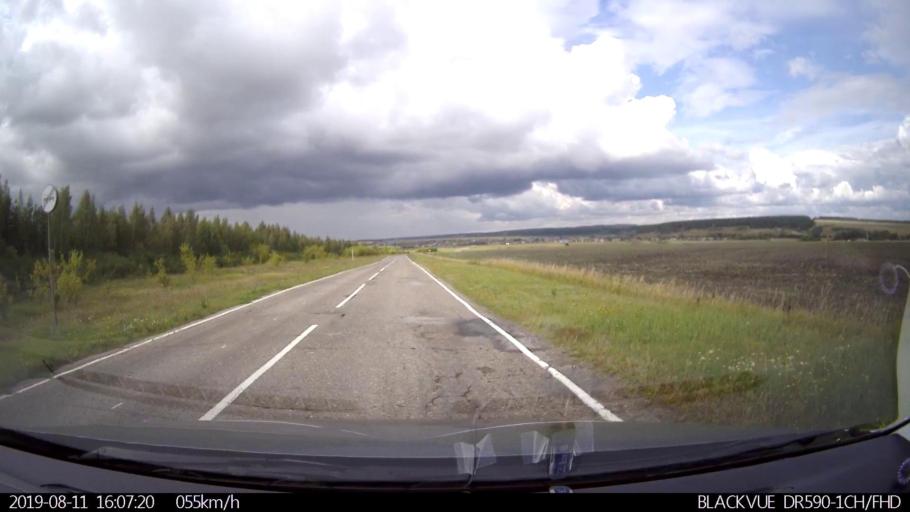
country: RU
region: Ulyanovsk
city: Ignatovka
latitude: 53.9758
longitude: 47.6475
